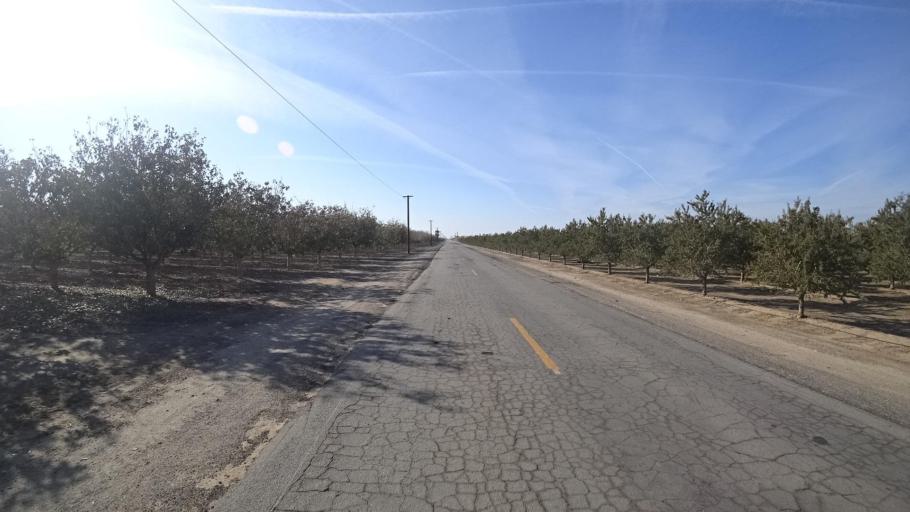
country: US
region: California
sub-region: Kern County
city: McFarland
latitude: 35.7032
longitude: -119.3174
